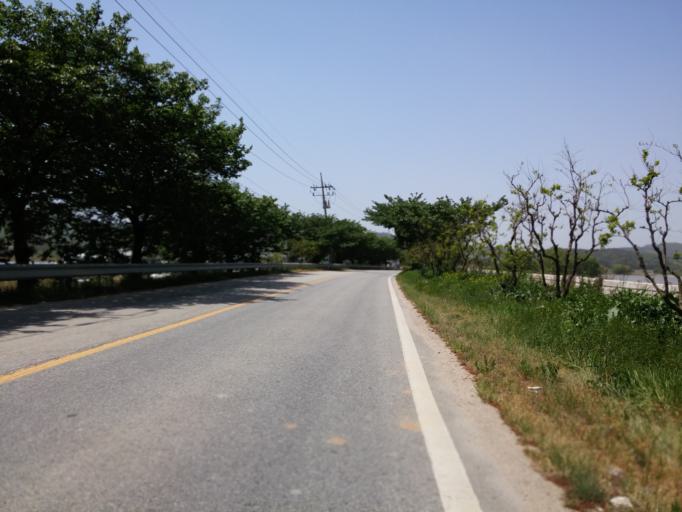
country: KR
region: Chungcheongnam-do
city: Nonsan
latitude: 36.2135
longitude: 127.1934
